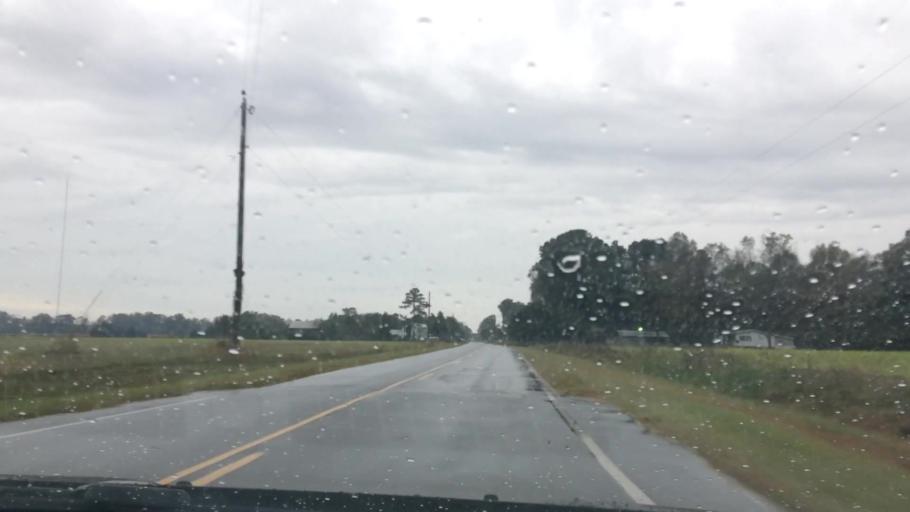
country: US
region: North Carolina
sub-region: Pitt County
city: Grifton
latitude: 35.3962
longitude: -77.3990
